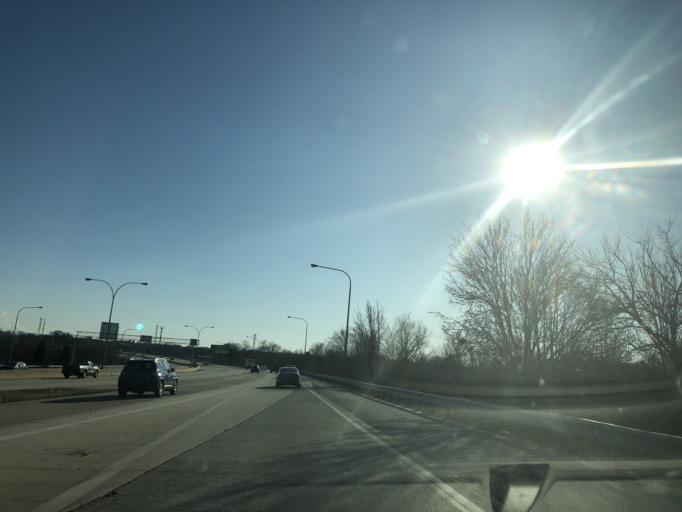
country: US
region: Delaware
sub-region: New Castle County
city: Elsmere
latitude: 39.7359
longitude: -75.6214
